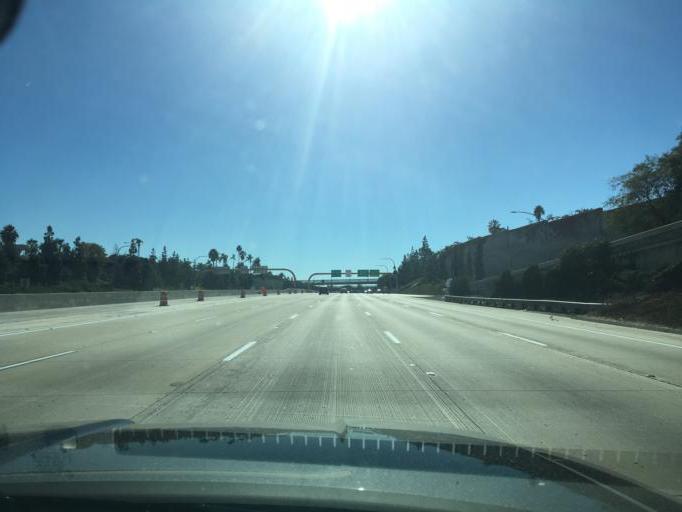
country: US
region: California
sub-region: San Diego County
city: San Diego
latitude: 32.7627
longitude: -117.1094
